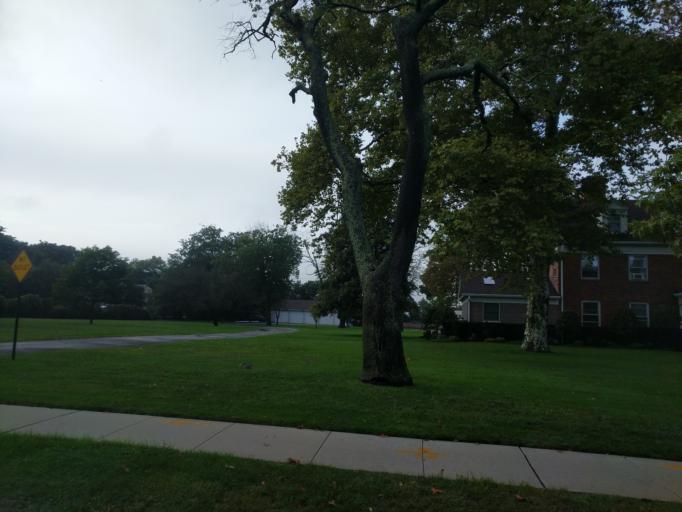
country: US
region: New York
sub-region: Nassau County
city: Lawrence
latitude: 40.6136
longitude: -73.7368
